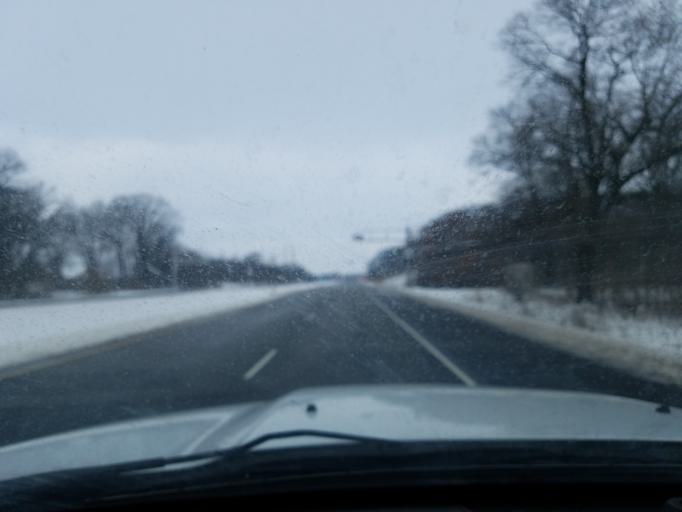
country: US
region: Indiana
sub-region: Marshall County
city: Argos
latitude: 41.2798
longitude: -86.2713
